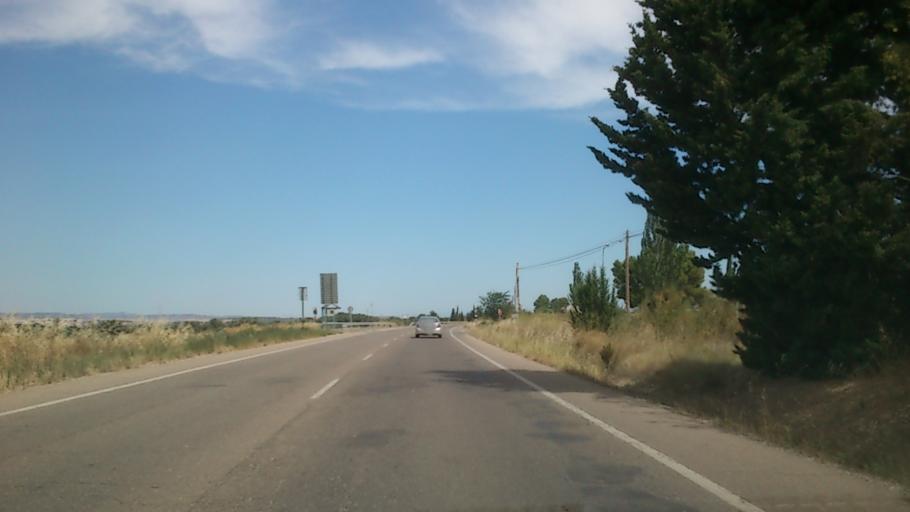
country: ES
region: Aragon
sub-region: Provincia de Zaragoza
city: Villanueva de Gallego
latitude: 41.7339
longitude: -0.8088
